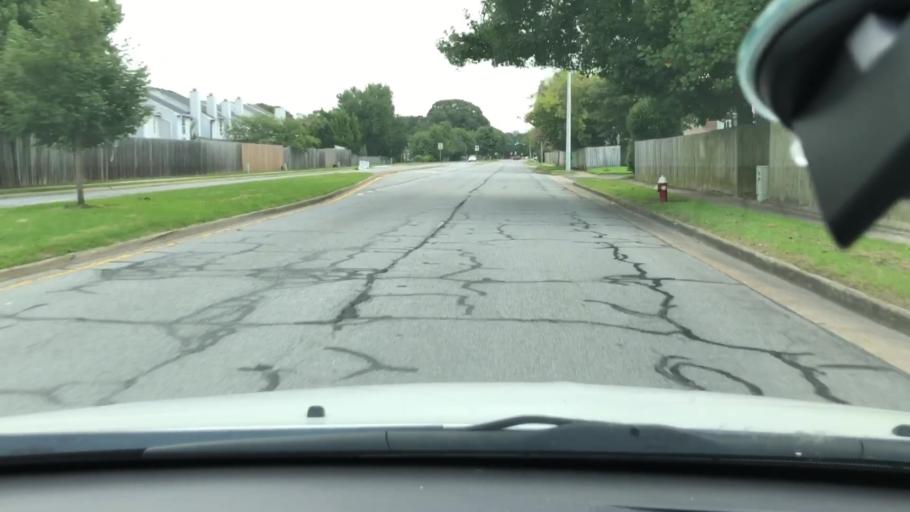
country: US
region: Virginia
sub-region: City of Chesapeake
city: Chesapeake
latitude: 36.8141
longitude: -76.1858
